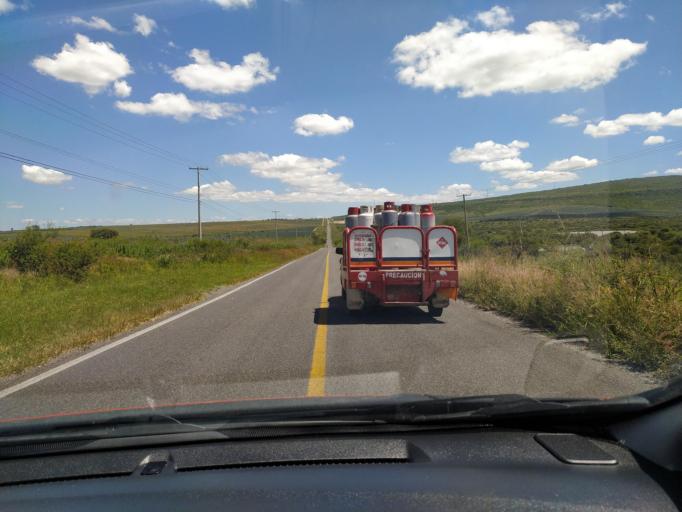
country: MX
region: Jalisco
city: San Diego de Alejandria
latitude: 21.0197
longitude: -101.9506
